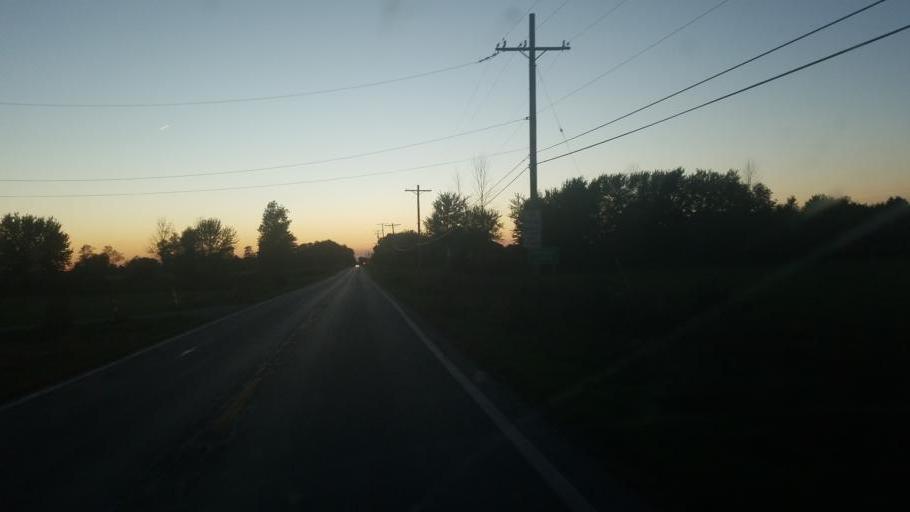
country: US
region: Ohio
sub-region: Ashtabula County
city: Jefferson
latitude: 41.7517
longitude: -80.6604
